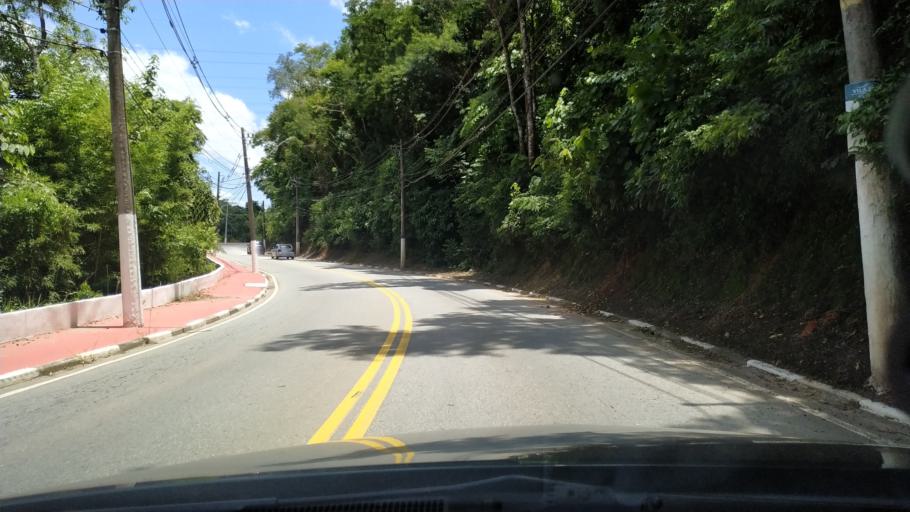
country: BR
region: Sao Paulo
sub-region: Santana De Parnaiba
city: Santana de Parnaiba
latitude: -23.4462
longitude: -46.9042
